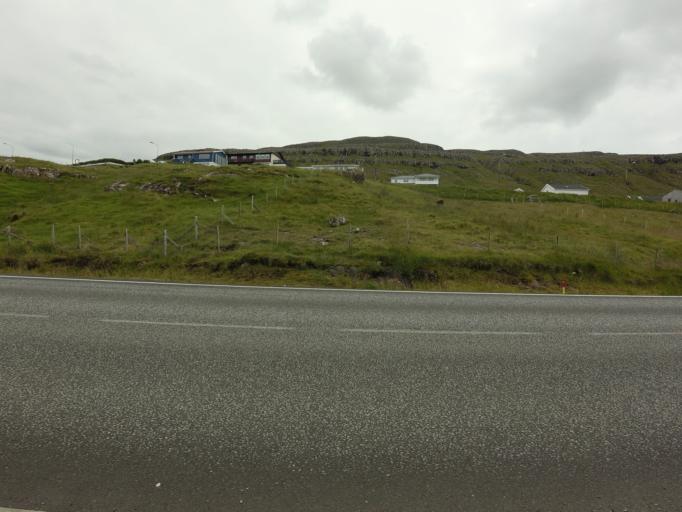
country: FO
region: Suduroy
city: Tvoroyri
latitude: 61.5479
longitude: -6.8183
